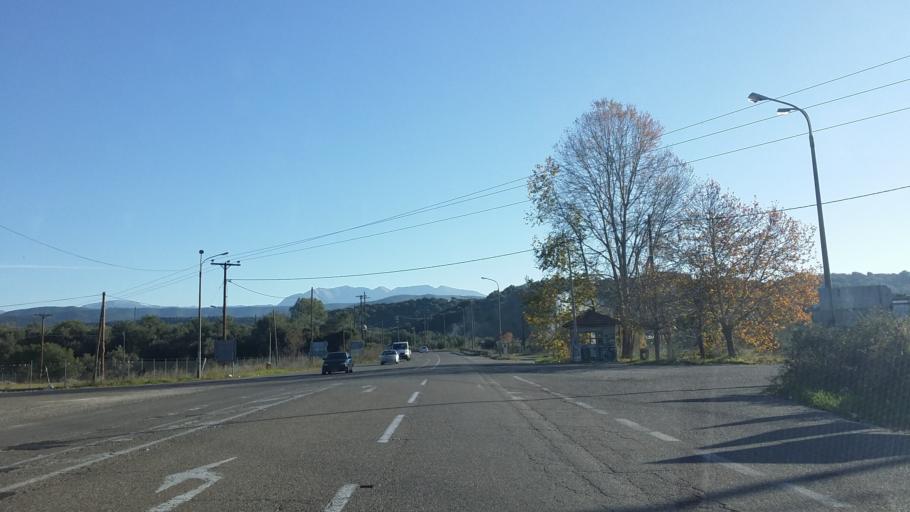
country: GR
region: West Greece
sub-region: Nomos Aitolias kai Akarnanias
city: Neapolis
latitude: 38.6699
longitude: 21.3418
